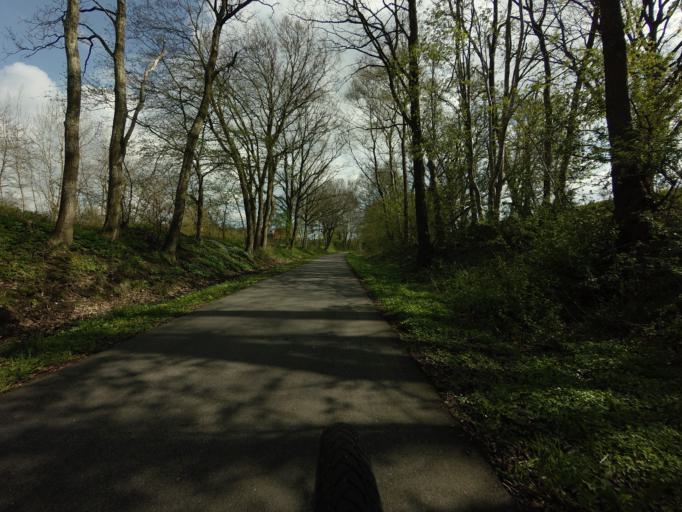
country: DK
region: North Denmark
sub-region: Mariagerfjord Kommune
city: Hadsund
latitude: 56.7355
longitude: 10.1548
